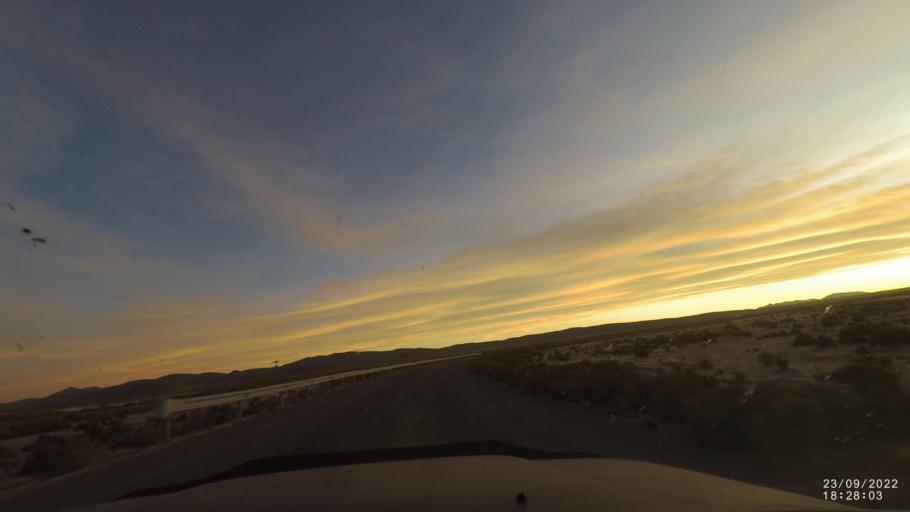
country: BO
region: Oruro
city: Challapata
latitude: -19.3341
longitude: -67.1730
